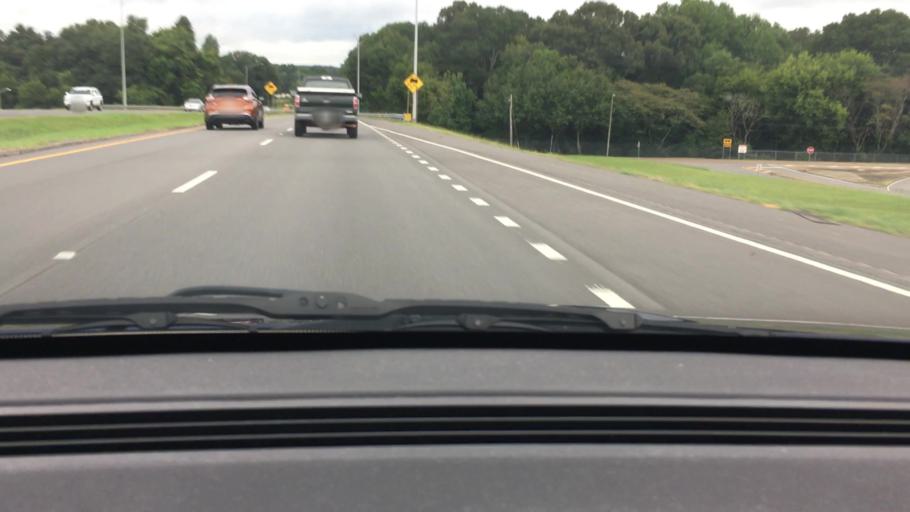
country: US
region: Alabama
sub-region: Tuscaloosa County
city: Tuscaloosa
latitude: 33.2145
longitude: -87.5275
